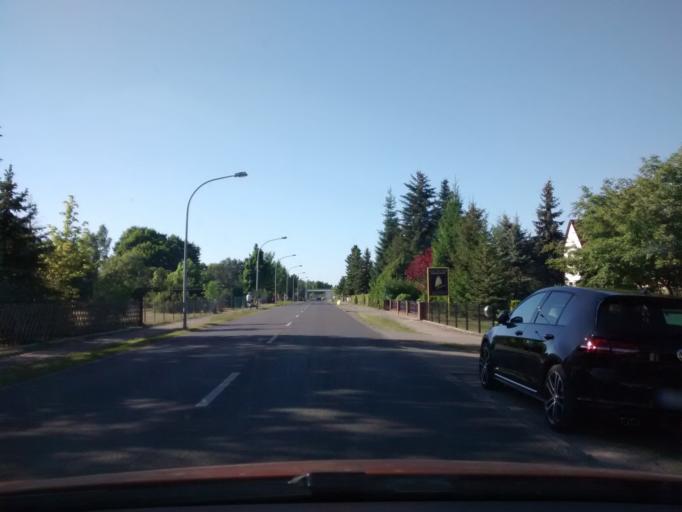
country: DE
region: Brandenburg
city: Langewahl
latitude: 52.3309
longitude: 14.0771
